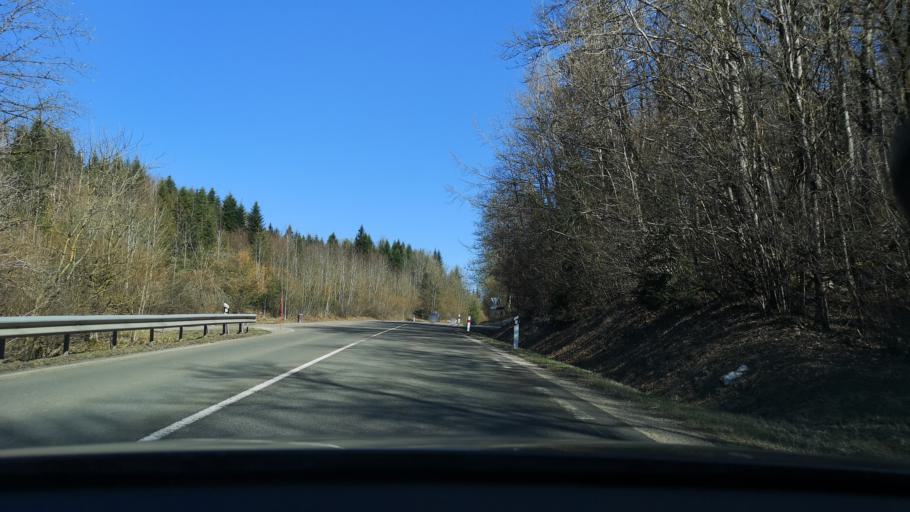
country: FR
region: Franche-Comte
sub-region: Departement du Doubs
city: Doubs
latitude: 46.9675
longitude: 6.3452
